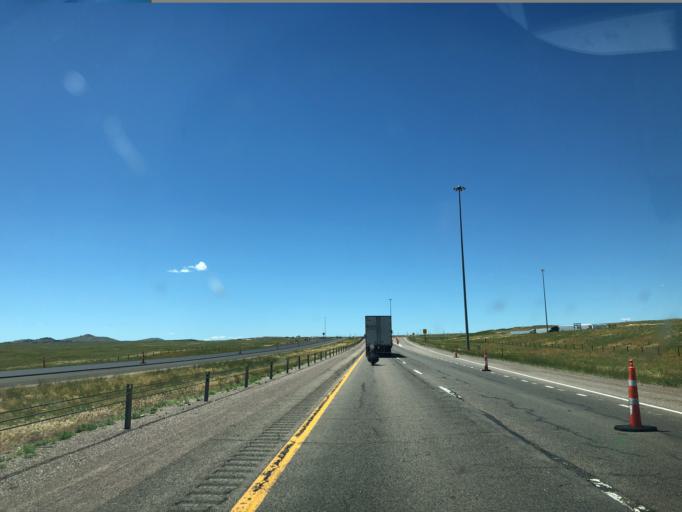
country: US
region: Wyoming
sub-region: Laramie County
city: Cheyenne
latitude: 41.0976
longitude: -105.1099
